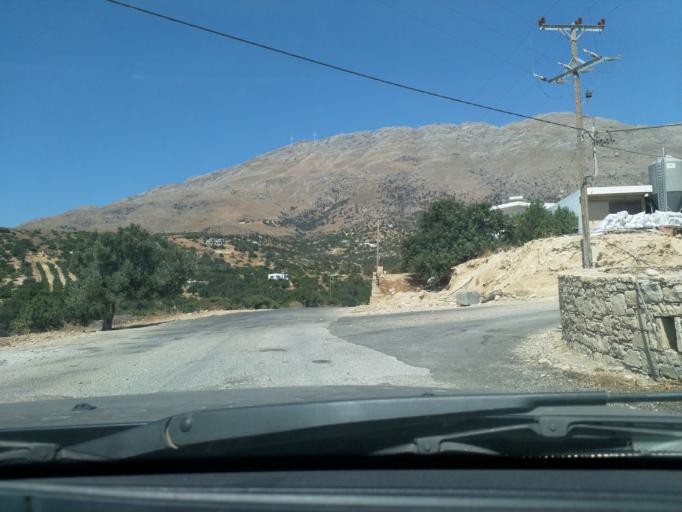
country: GR
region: Crete
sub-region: Nomos Rethymnis
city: Agia Galini
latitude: 35.1218
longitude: 24.5585
